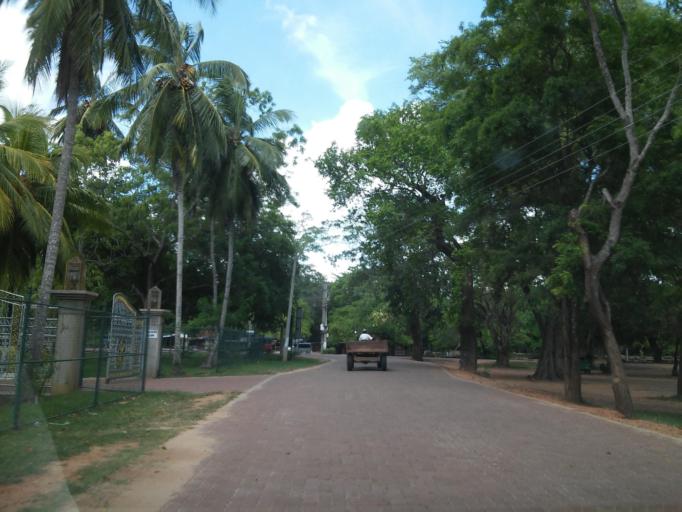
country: LK
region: North Central
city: Anuradhapura
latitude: 8.3693
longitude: 80.3944
